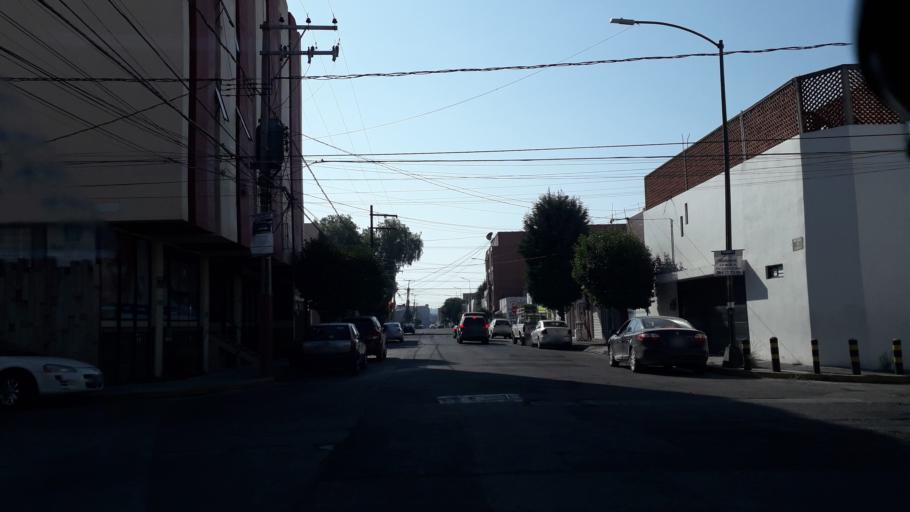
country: MX
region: Puebla
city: Puebla
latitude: 19.0323
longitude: -98.2144
